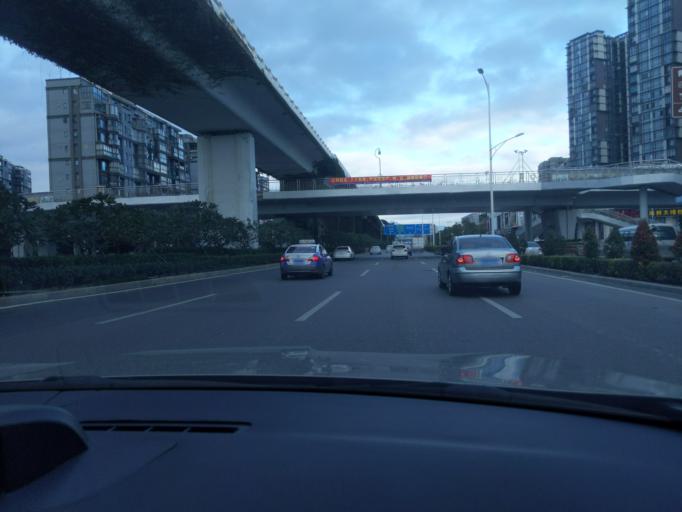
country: CN
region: Fujian
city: Yingcun
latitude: 24.5863
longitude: 118.1067
